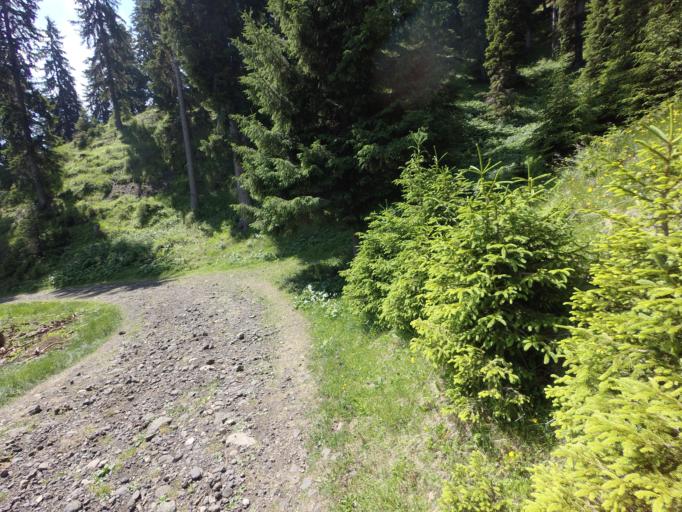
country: IT
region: Trentino-Alto Adige
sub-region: Bolzano
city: Ortisei
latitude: 46.5212
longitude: 11.6597
